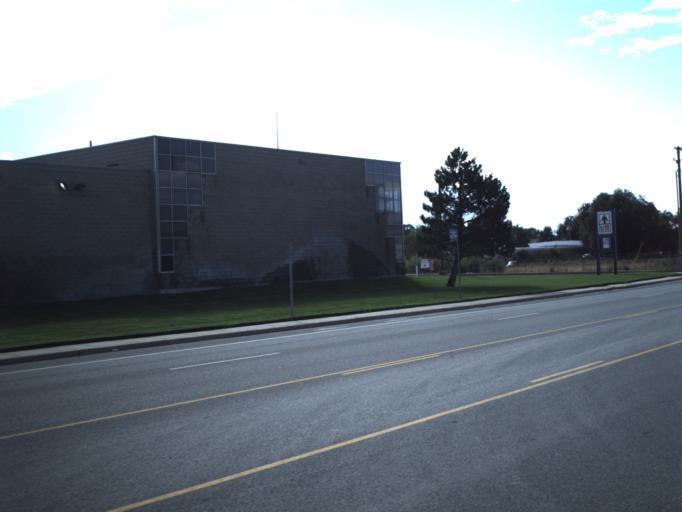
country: US
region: Utah
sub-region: Salt Lake County
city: Salt Lake City
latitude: 40.7483
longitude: -111.9391
